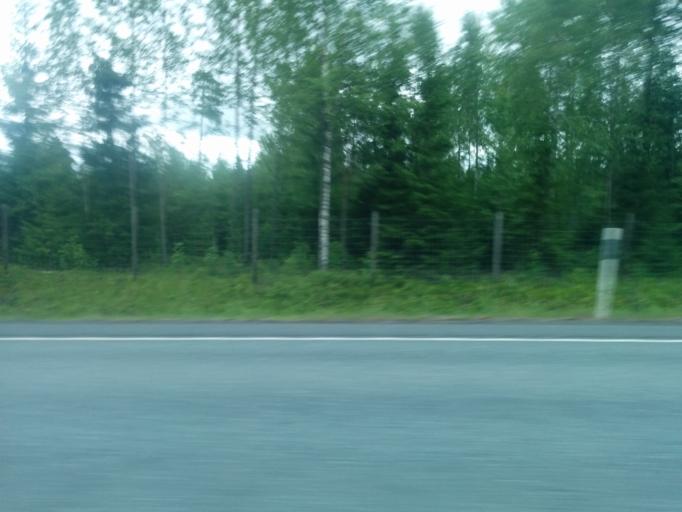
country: FI
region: Pirkanmaa
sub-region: Tampere
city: Orivesi
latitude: 61.6622
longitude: 24.2626
